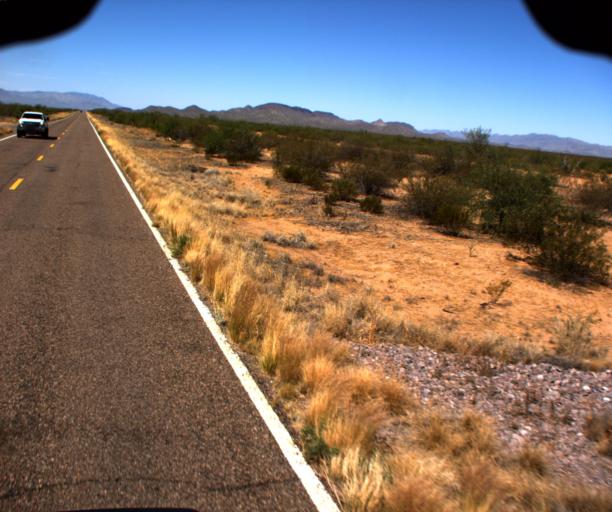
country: US
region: Arizona
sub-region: Yavapai County
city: Congress
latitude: 34.0766
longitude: -113.0256
